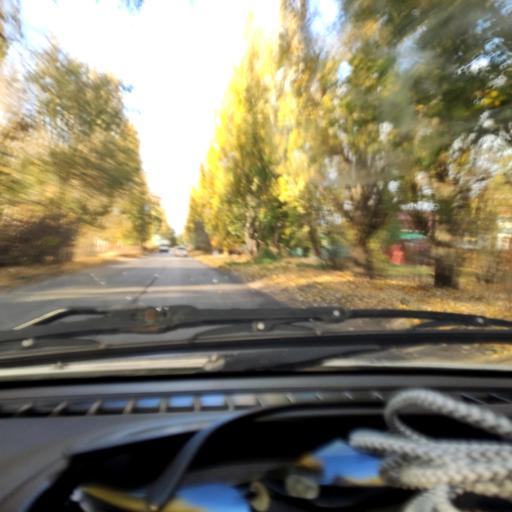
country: RU
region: Samara
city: Tol'yatti
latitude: 53.5323
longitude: 49.4183
